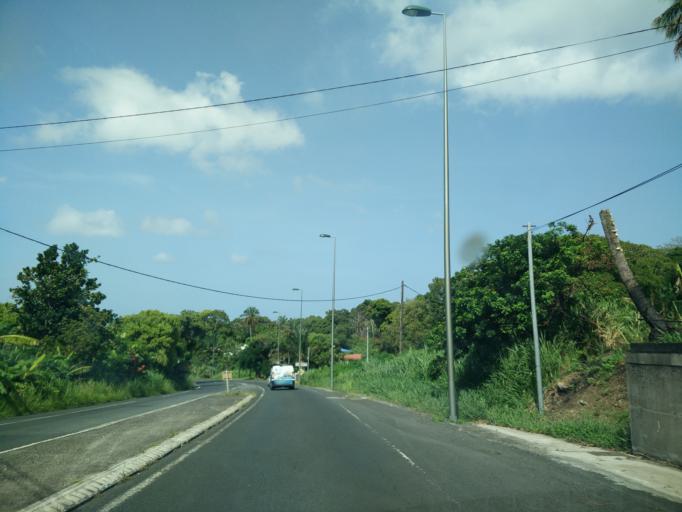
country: GP
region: Guadeloupe
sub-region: Guadeloupe
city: Gourbeyre
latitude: 16.0017
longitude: -61.6979
